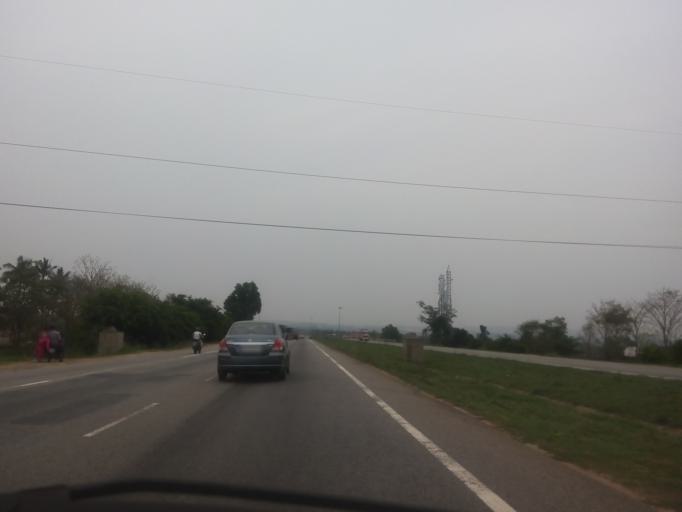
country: IN
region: Karnataka
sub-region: Bangalore Urban
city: Bangalore
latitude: 12.8607
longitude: 77.5205
